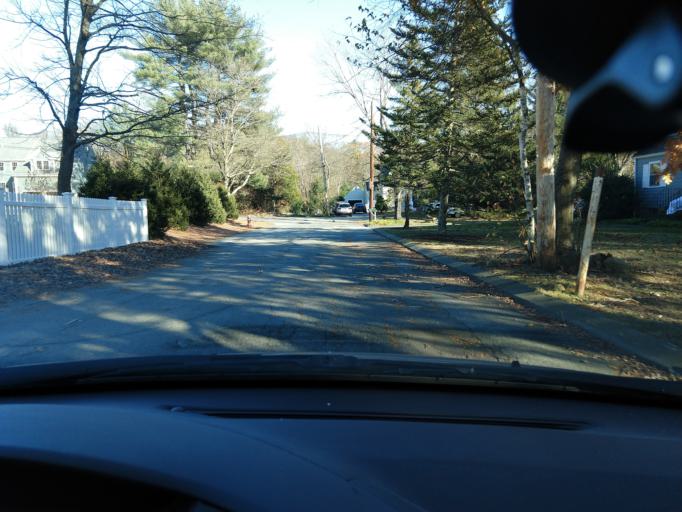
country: US
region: Massachusetts
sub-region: Middlesex County
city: Bedford
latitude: 42.5173
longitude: -71.2879
